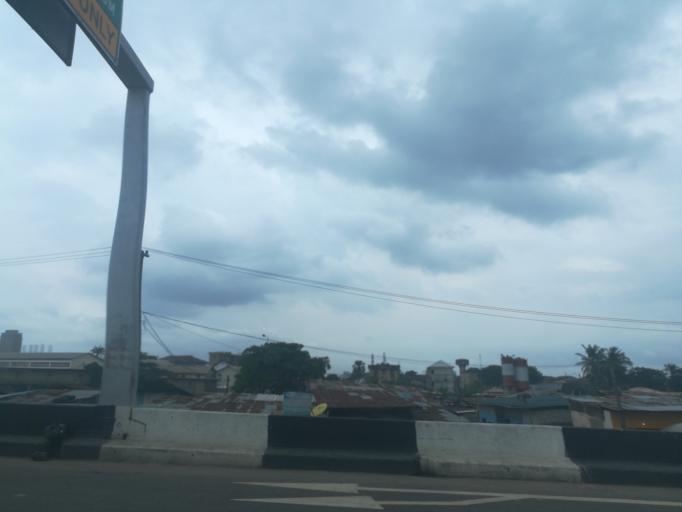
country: NG
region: Lagos
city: Lagos
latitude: 6.4531
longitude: 3.4085
